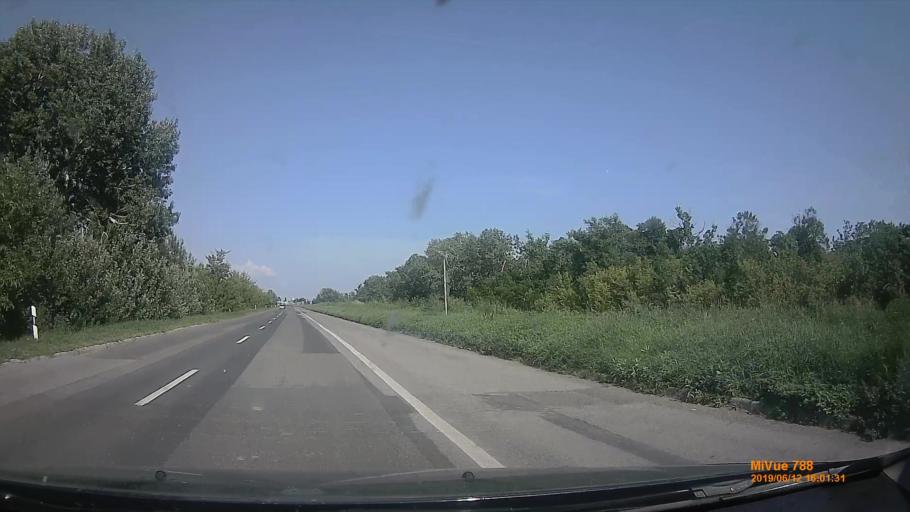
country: RO
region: Arad
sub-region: Comuna Nadlac
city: Nadlac
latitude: 46.1675
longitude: 20.6977
